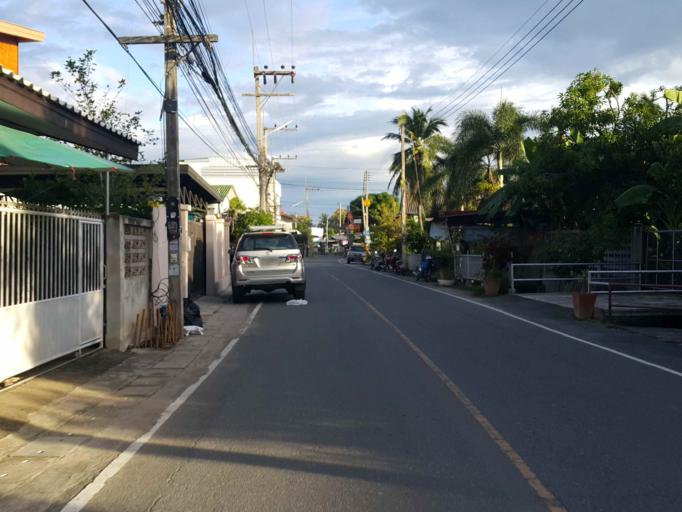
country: TH
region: Chiang Mai
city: Chiang Mai
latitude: 18.7757
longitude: 99.0413
